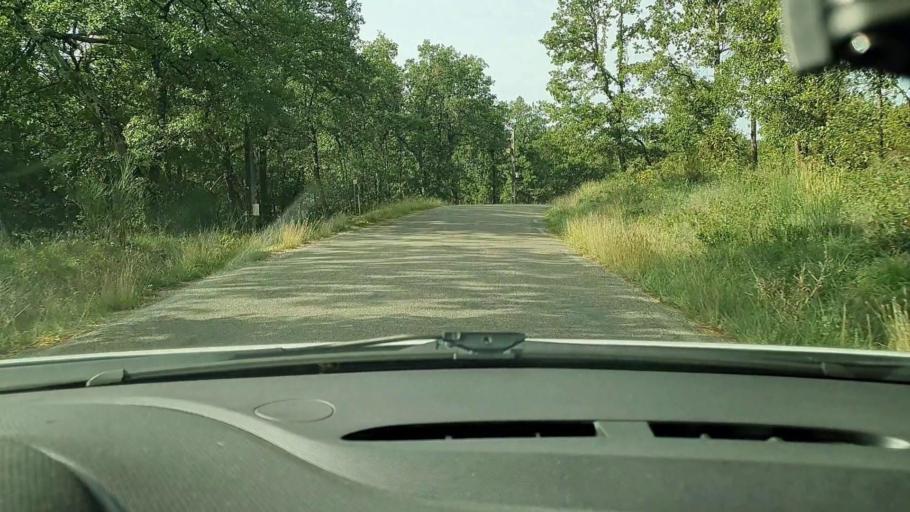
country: FR
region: Languedoc-Roussillon
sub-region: Departement du Gard
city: Saint-Quentin-la-Poterie
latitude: 44.1096
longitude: 4.4260
